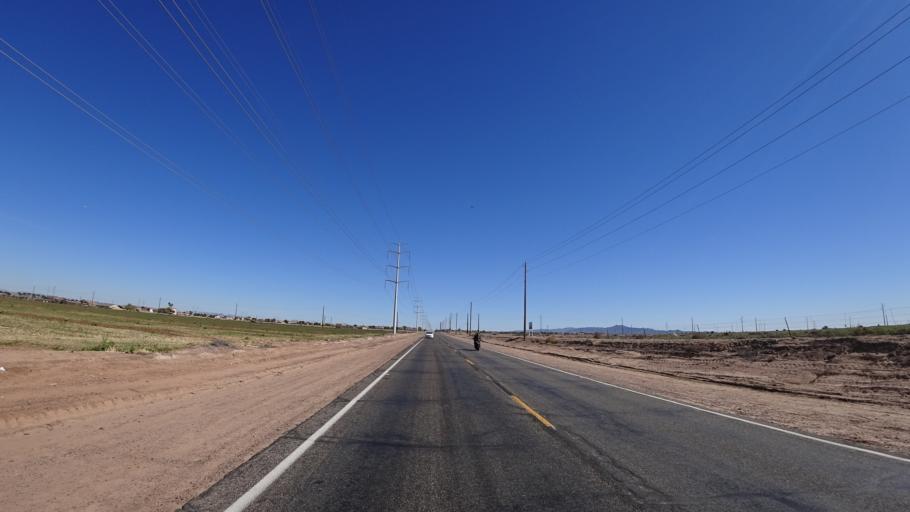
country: US
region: Arizona
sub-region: Maricopa County
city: Tolleson
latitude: 33.4064
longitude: -112.2933
